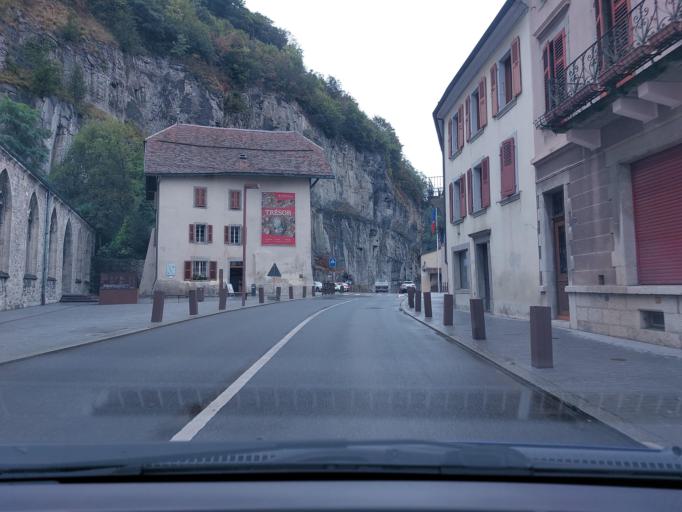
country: CH
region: Valais
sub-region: Saint-Maurice District
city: Saint-Maurice
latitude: 46.2195
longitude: 7.0041
